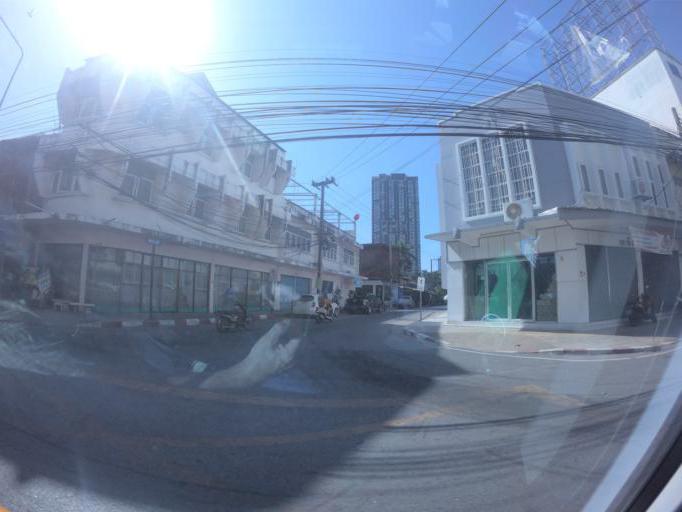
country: TH
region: Khon Kaen
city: Khon Kaen
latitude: 16.4798
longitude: 102.9592
